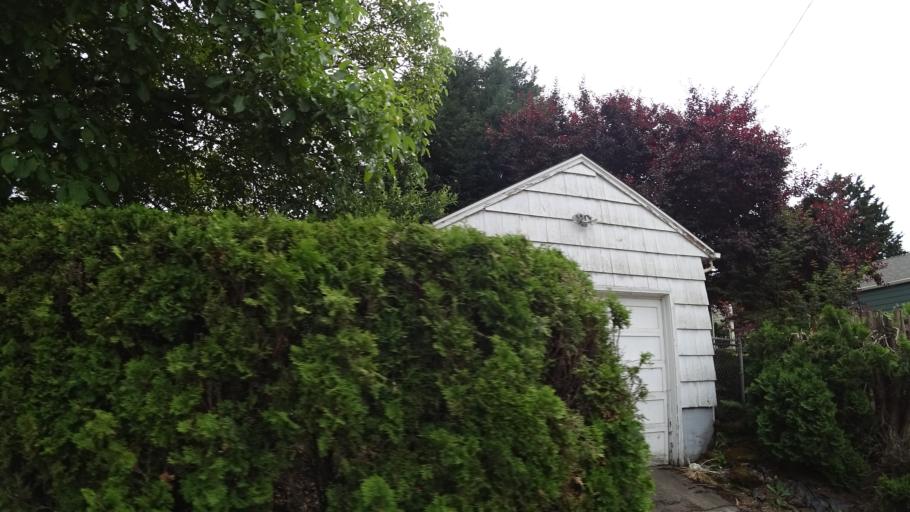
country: US
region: Oregon
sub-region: Multnomah County
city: Portland
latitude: 45.5678
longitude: -122.6893
